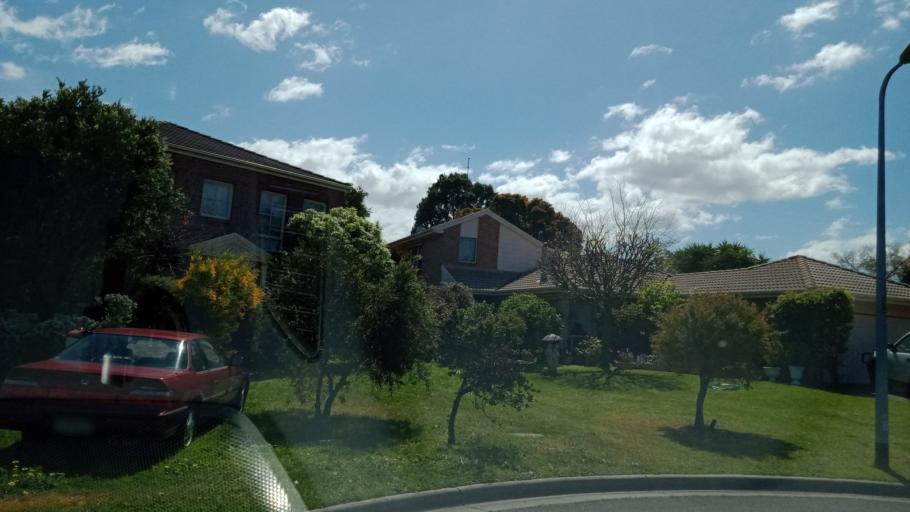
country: AU
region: Victoria
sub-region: Kingston
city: Chelsea Heights
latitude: -38.0378
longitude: 145.1329
